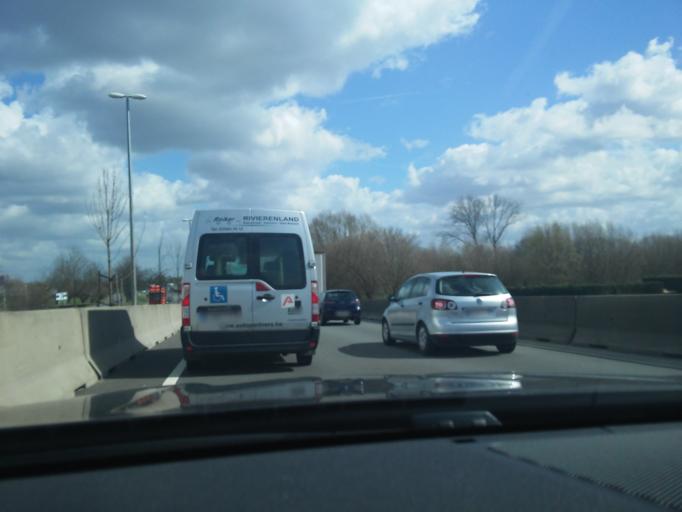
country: BE
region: Flanders
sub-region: Provincie Antwerpen
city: Willebroek
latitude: 51.0614
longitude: 4.3272
